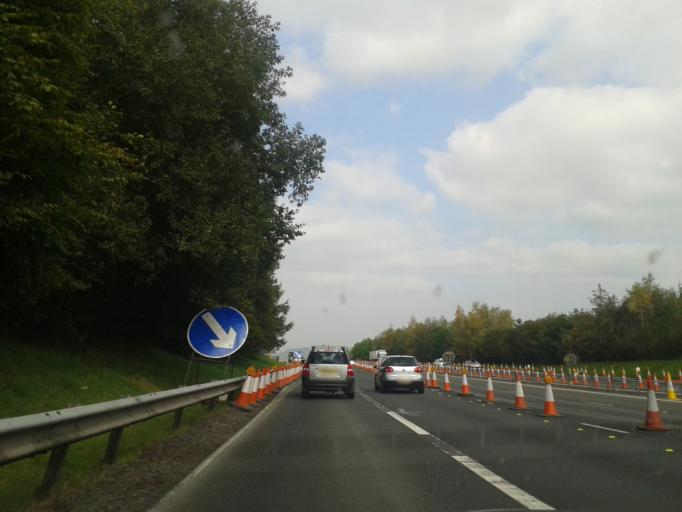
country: GB
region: Scotland
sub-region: Dumfries and Galloway
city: Moffat
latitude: 55.2393
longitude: -3.4100
